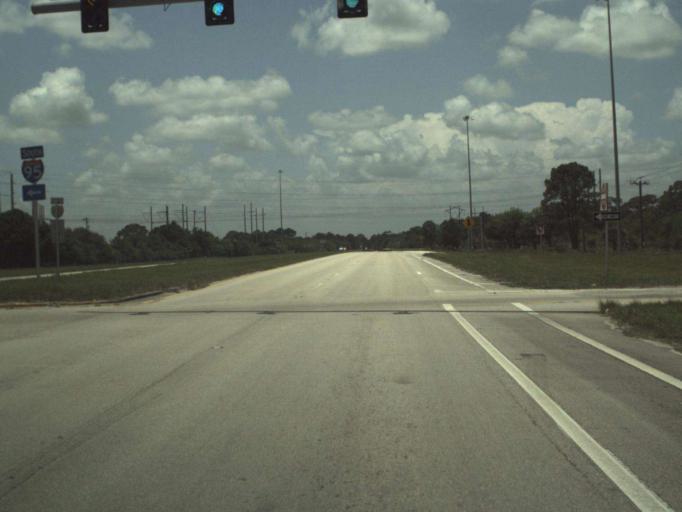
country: US
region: Florida
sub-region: Saint Lucie County
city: Fort Pierce South
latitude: 27.3746
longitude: -80.4118
